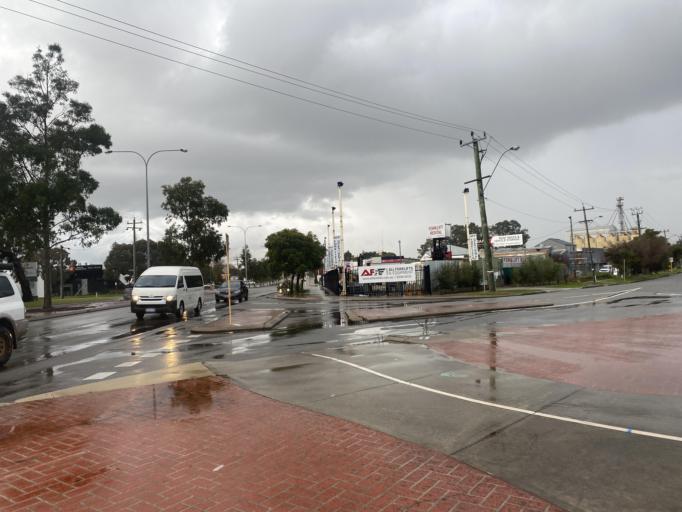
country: AU
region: Western Australia
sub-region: Canning
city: Bentley
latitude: -31.9942
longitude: 115.9225
